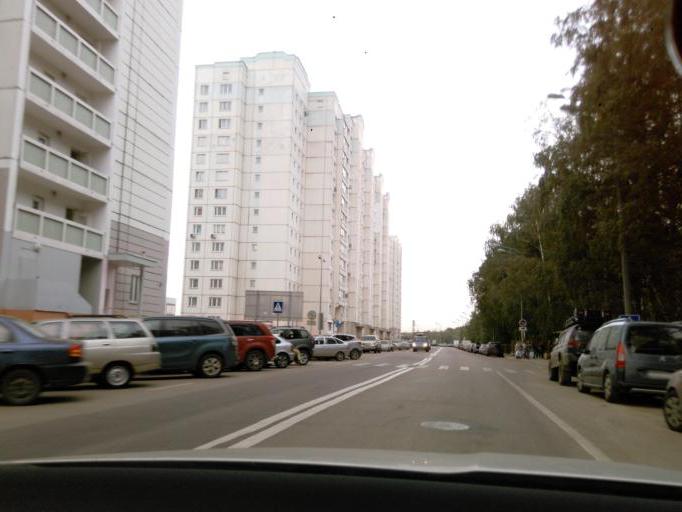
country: RU
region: Moscow
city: Severnyy
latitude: 55.9288
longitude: 37.5435
